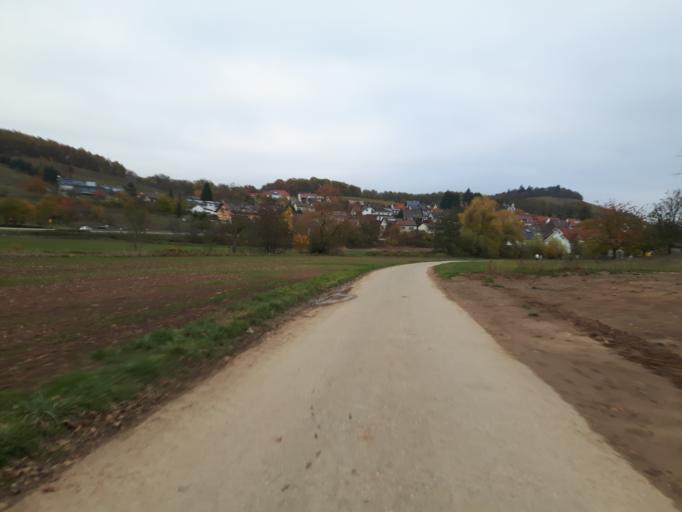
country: DE
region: Baden-Wuerttemberg
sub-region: Karlsruhe Region
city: Zaisenhausen
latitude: 49.1747
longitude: 8.7855
